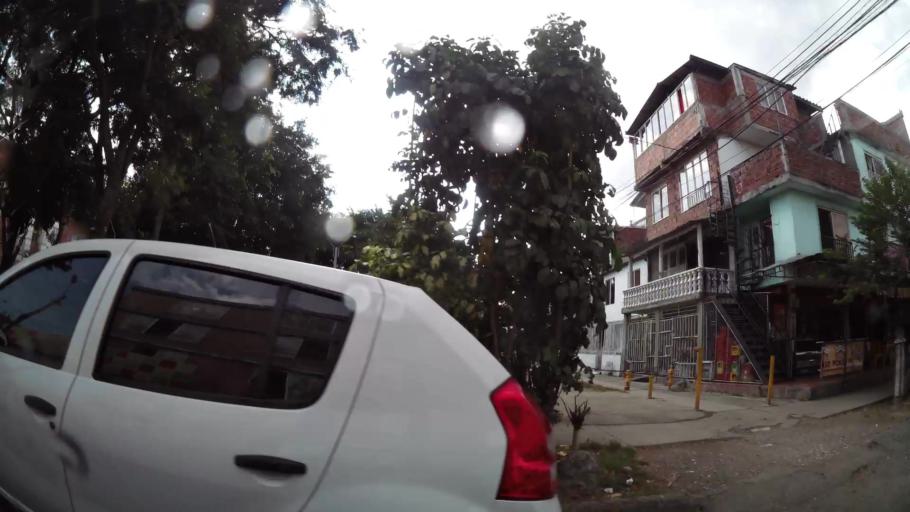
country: CO
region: Valle del Cauca
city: Cali
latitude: 3.4671
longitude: -76.4869
